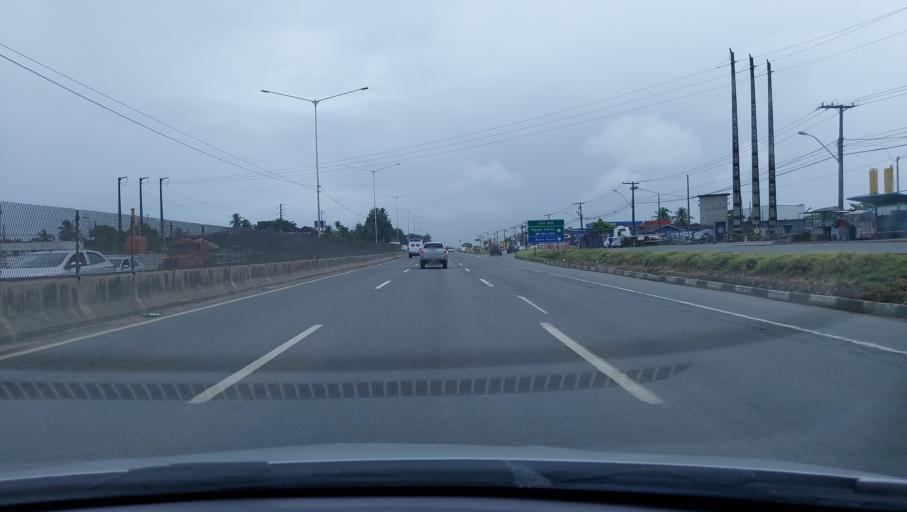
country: BR
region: Bahia
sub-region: Salvador
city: Salvador
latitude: -12.8961
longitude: -38.4486
